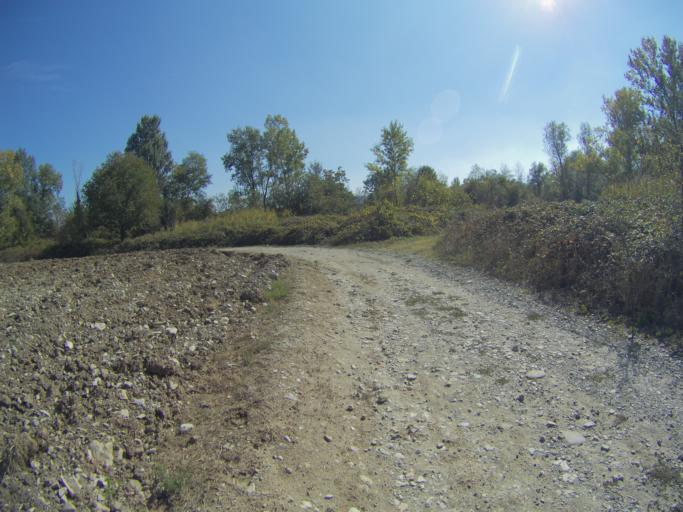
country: IT
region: Emilia-Romagna
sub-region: Provincia di Reggio Emilia
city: Forche
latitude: 44.6305
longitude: 10.5785
